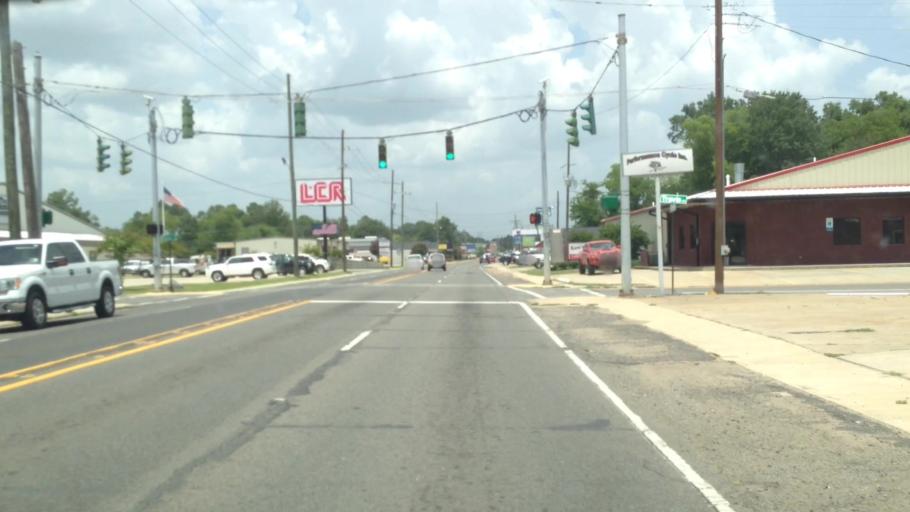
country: US
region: Louisiana
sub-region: Ouachita Parish
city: West Monroe
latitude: 32.5118
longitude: -92.1351
